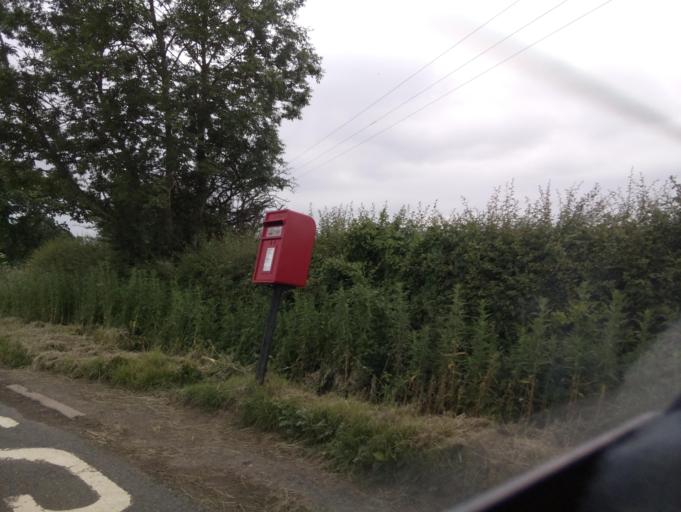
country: GB
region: England
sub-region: Leicestershire
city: Melton Mowbray
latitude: 52.7168
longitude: -0.8295
